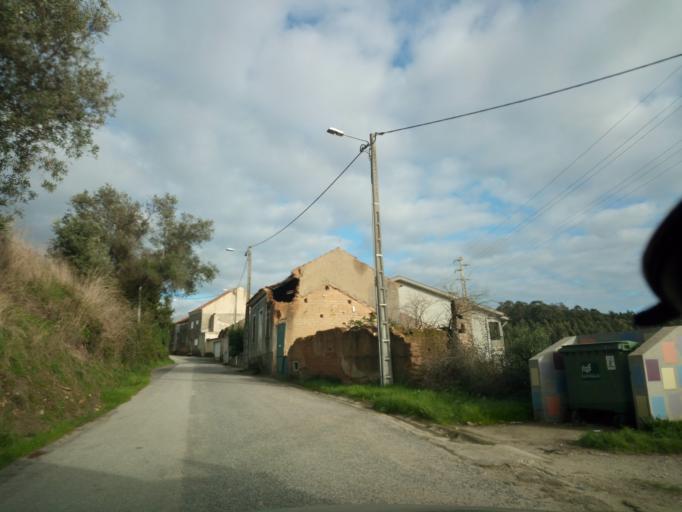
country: PT
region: Aveiro
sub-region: Oliveira do Bairro
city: Oliveira do Bairro
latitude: 40.5415
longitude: -8.4905
